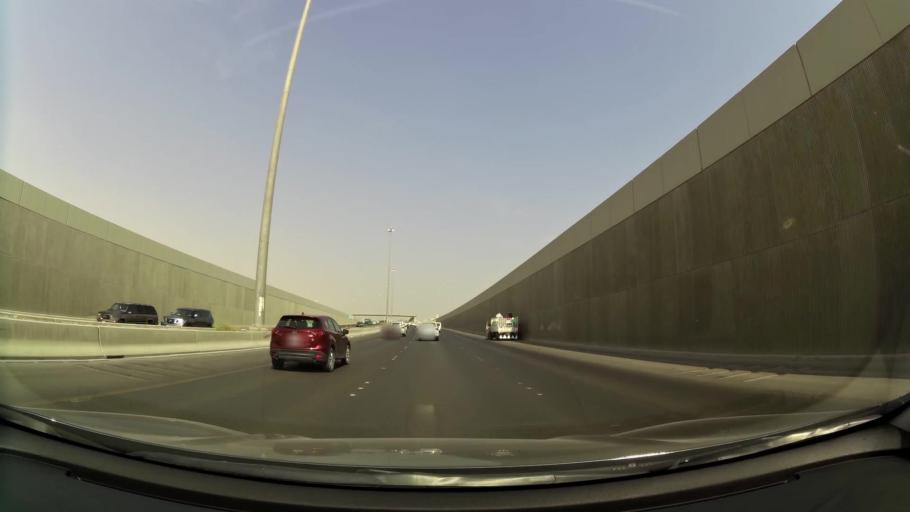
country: KW
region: Al Ahmadi
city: Al Manqaf
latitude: 29.1075
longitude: 48.1184
